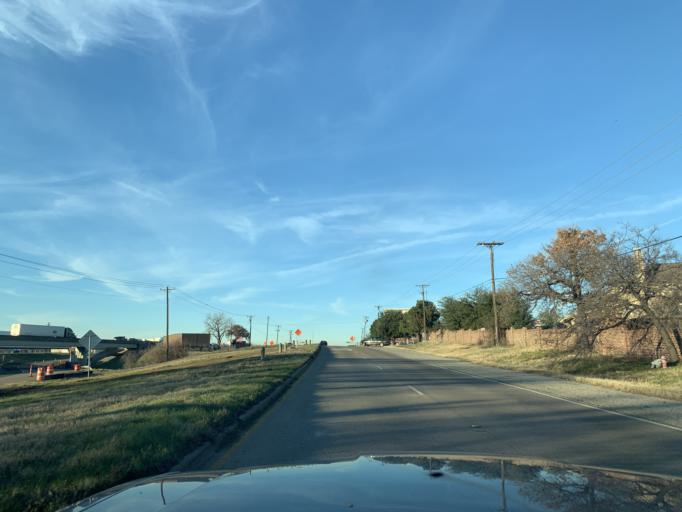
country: US
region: Texas
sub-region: Tarrant County
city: Euless
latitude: 32.8677
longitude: -97.0998
